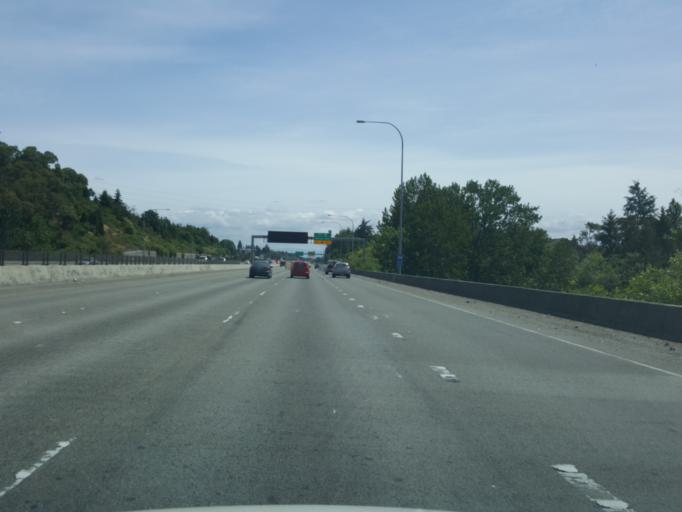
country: US
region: Washington
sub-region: Pierce County
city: Fircrest
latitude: 47.2346
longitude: -122.4934
